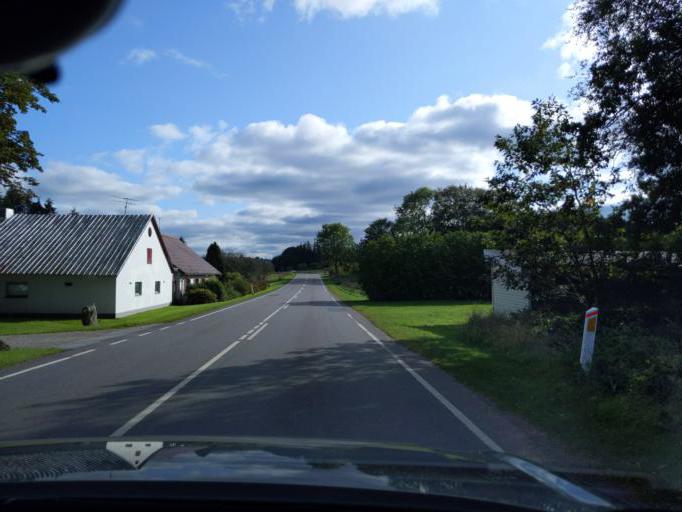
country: DK
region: North Denmark
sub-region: Mariagerfjord Kommune
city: Hobro
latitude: 56.5598
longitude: 9.7234
